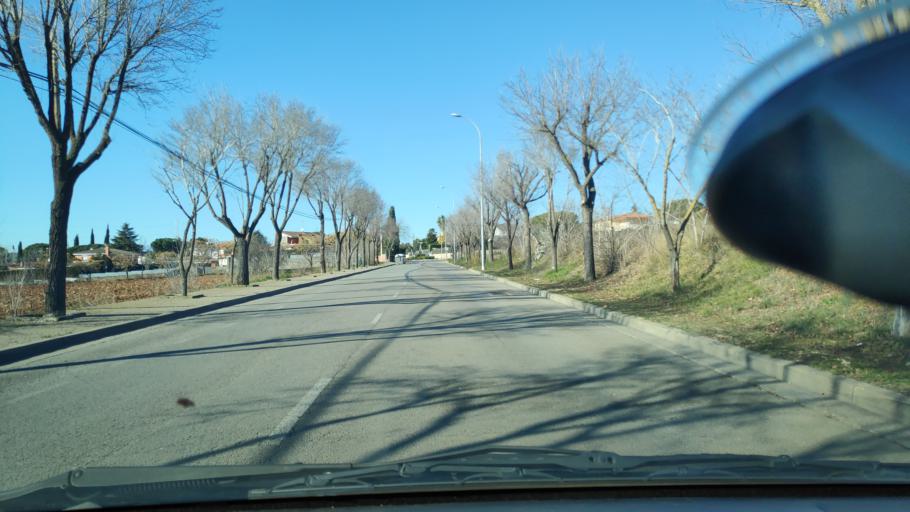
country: ES
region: Catalonia
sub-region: Provincia de Barcelona
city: Sant Quirze del Valles
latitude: 41.5377
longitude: 2.0681
